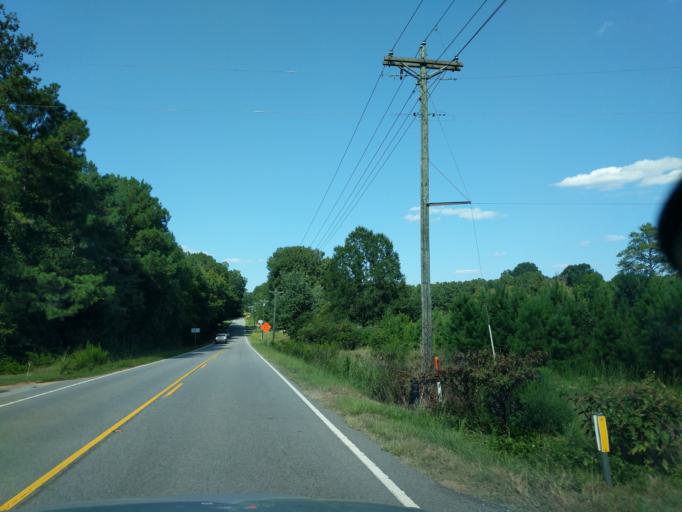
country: US
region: South Carolina
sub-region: Newberry County
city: Prosperity
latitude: 34.1428
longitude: -81.5343
